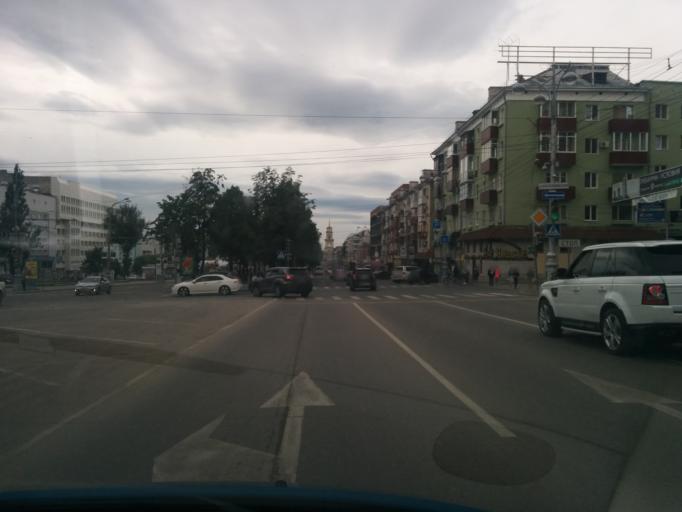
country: RU
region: Perm
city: Perm
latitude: 58.0090
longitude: 56.2412
